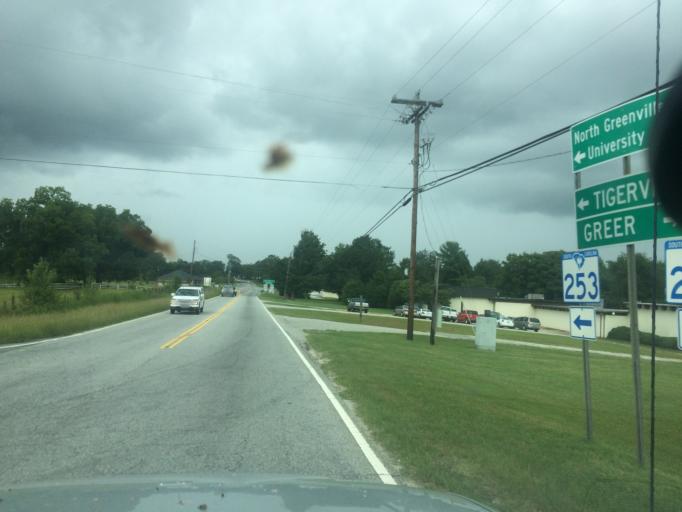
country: US
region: South Carolina
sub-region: Greenville County
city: Tigerville
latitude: 34.9917
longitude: -82.3431
